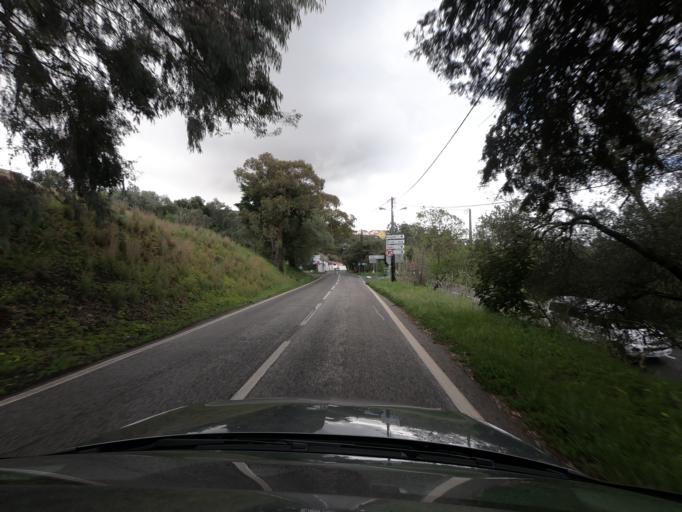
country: PT
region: Lisbon
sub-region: Oeiras
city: Quejas
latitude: 38.7372
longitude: -9.2603
